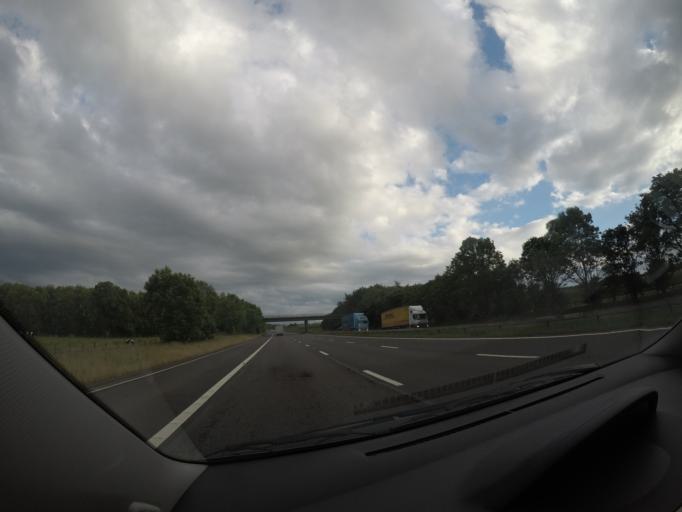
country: GB
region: England
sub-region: Cumbria
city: Penrith
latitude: 54.7239
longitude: -2.8005
